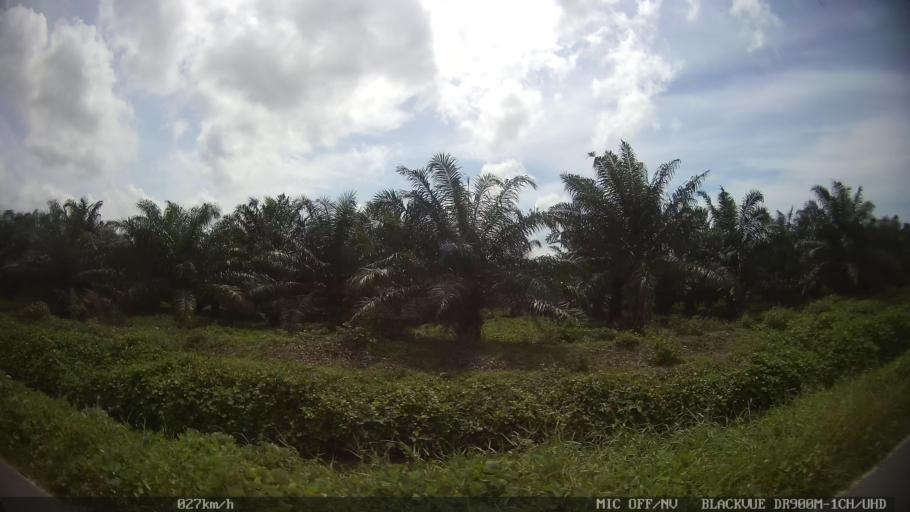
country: ID
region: North Sumatra
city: Percut
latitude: 3.5972
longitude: 98.8392
